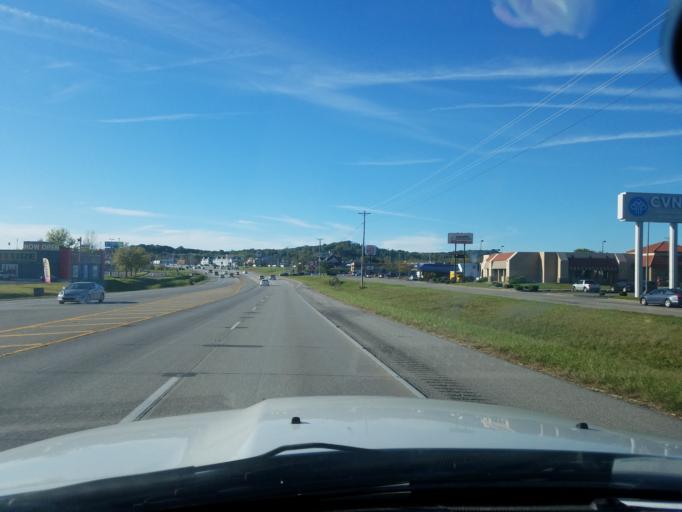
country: US
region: Kentucky
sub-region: Laurel County
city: London
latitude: 37.1093
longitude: -84.0896
